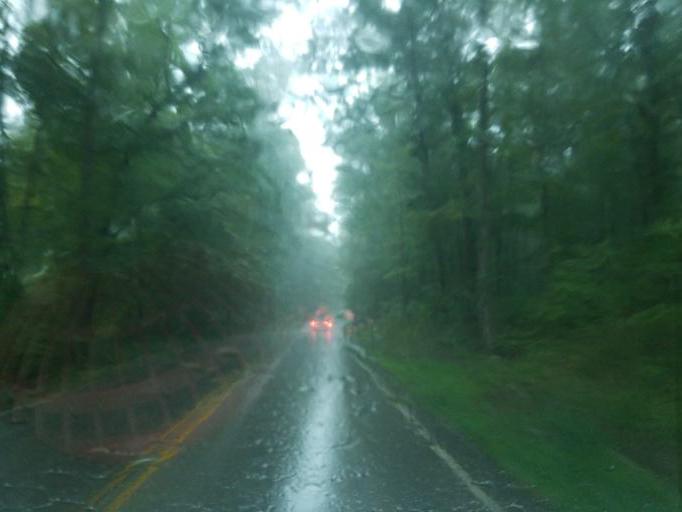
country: US
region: Kentucky
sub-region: Carter County
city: Olive Hill
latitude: 38.3467
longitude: -83.2025
